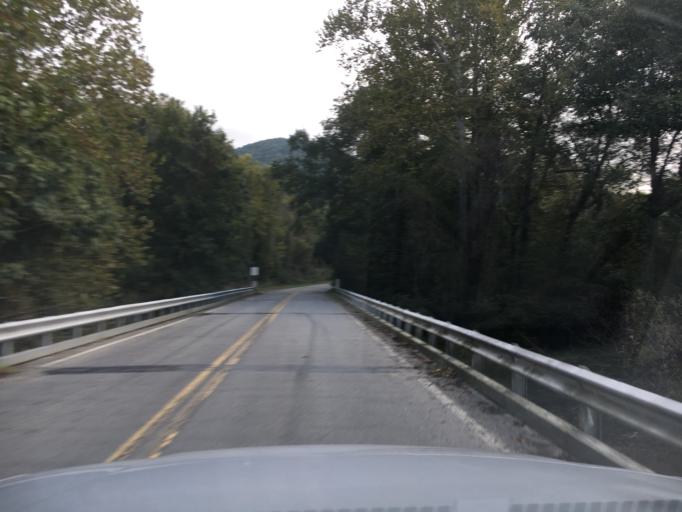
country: US
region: North Carolina
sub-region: Buncombe County
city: Swannanoa
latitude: 35.6077
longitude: -82.4199
